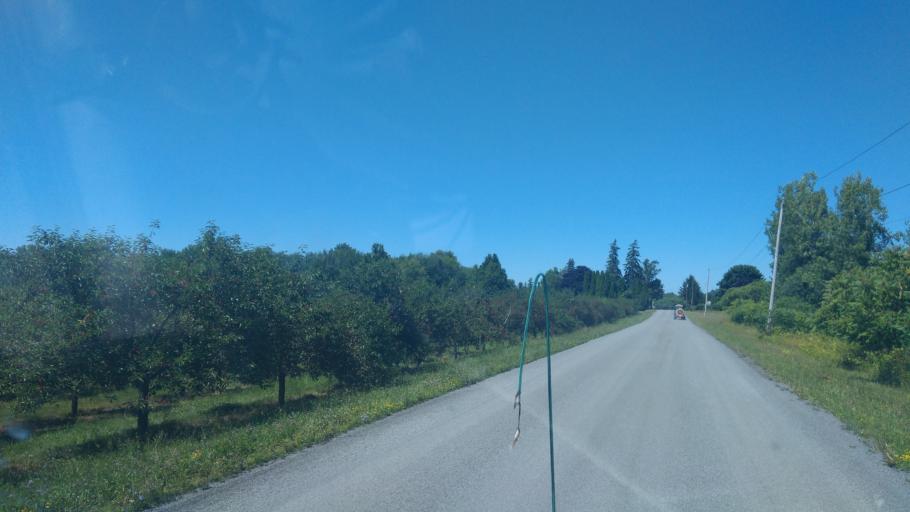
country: US
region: New York
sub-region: Wayne County
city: Lyons
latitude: 43.1649
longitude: -76.9779
